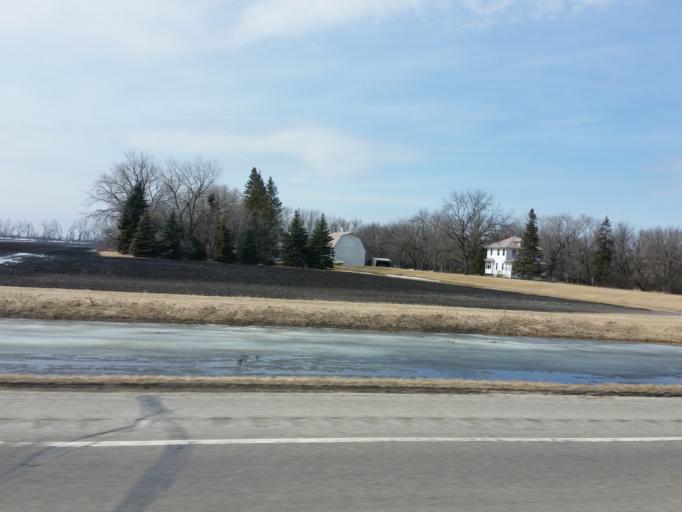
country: US
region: North Dakota
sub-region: Walsh County
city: Grafton
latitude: 48.3815
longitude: -97.4051
